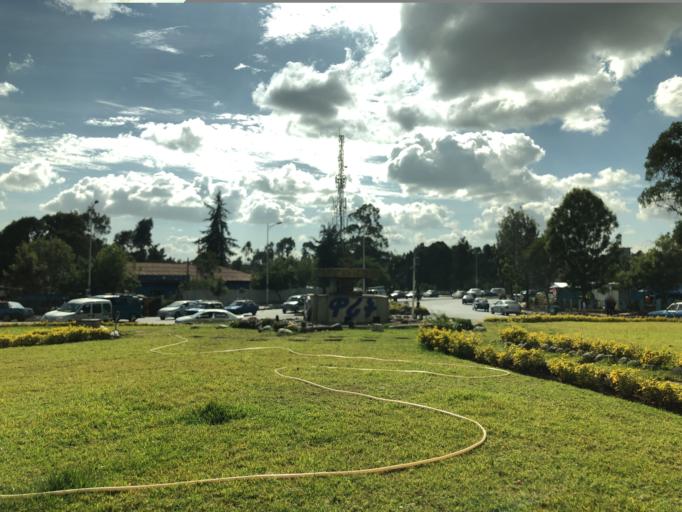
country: ET
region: Adis Abeba
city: Addis Ababa
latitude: 9.0235
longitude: 38.7810
